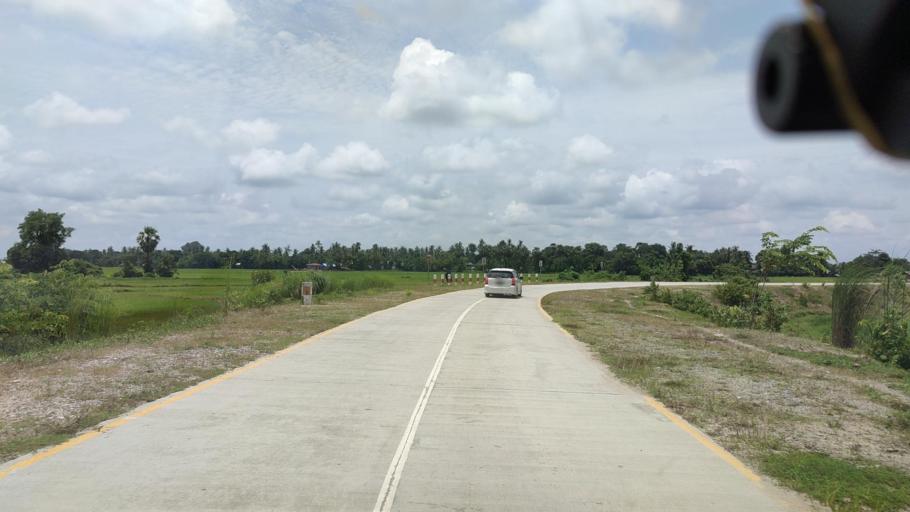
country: MM
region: Bago
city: Taungoo
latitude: 19.1345
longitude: 96.4369
